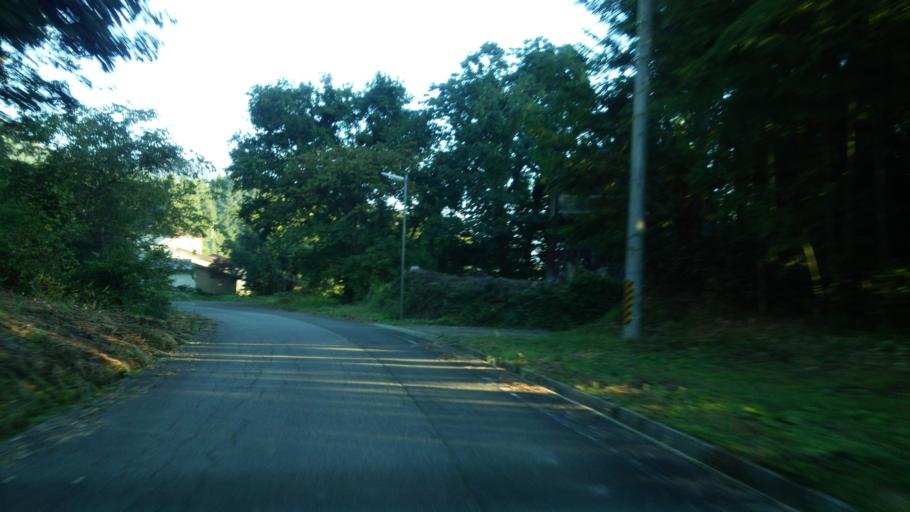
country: JP
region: Fukushima
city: Kitakata
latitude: 37.4315
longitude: 139.7997
